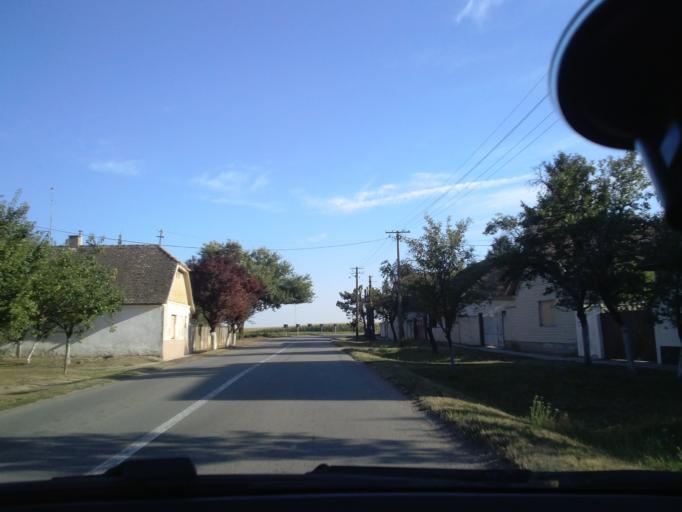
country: RS
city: Doroslovo
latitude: 45.5946
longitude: 19.1922
